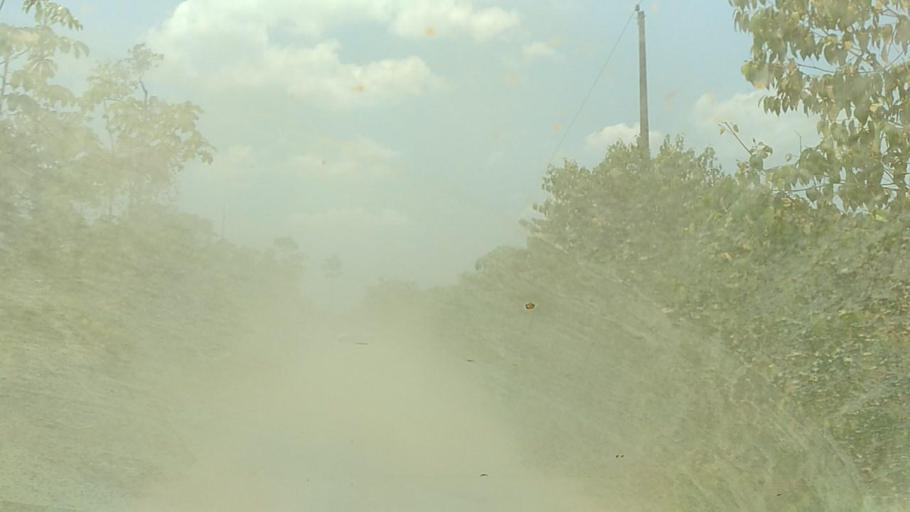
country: BR
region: Rondonia
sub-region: Porto Velho
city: Porto Velho
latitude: -8.7286
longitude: -63.2979
